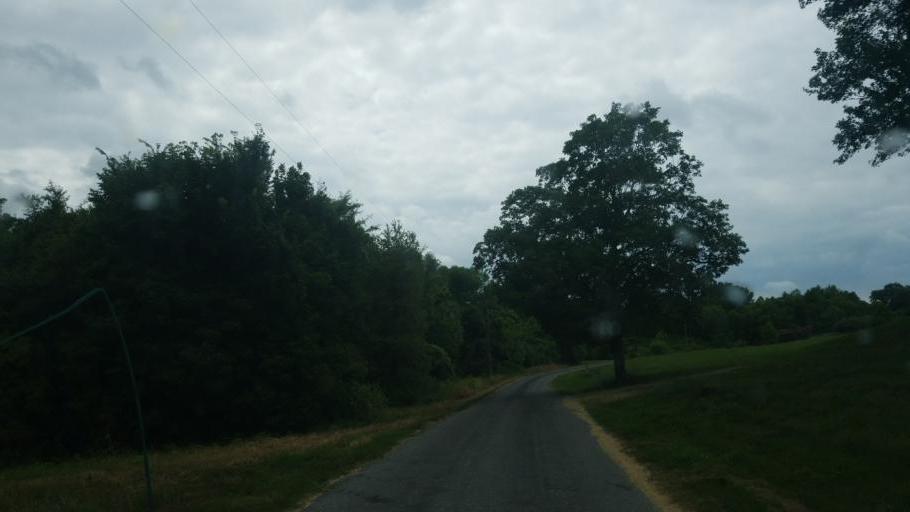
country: US
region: Illinois
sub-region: Jackson County
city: Murphysboro
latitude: 37.7018
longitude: -89.3414
